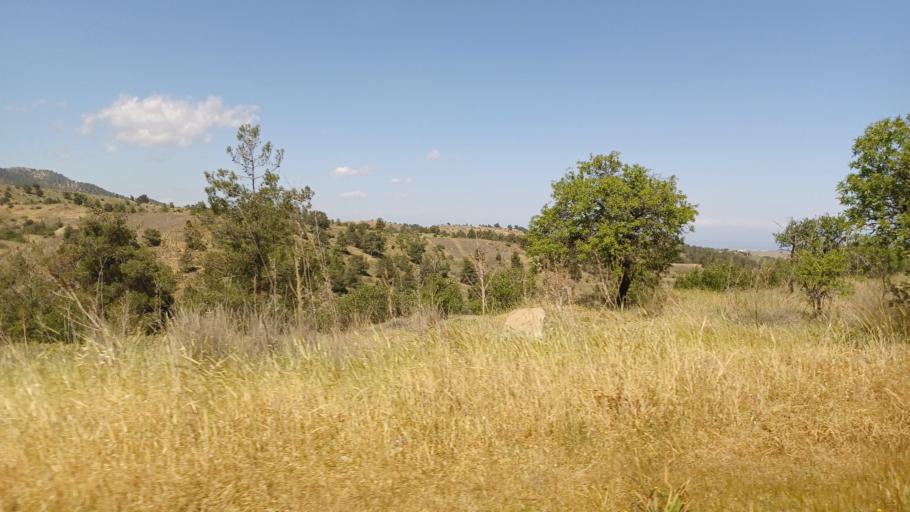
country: CY
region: Lefkosia
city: Astromeritis
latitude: 35.0588
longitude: 33.0235
